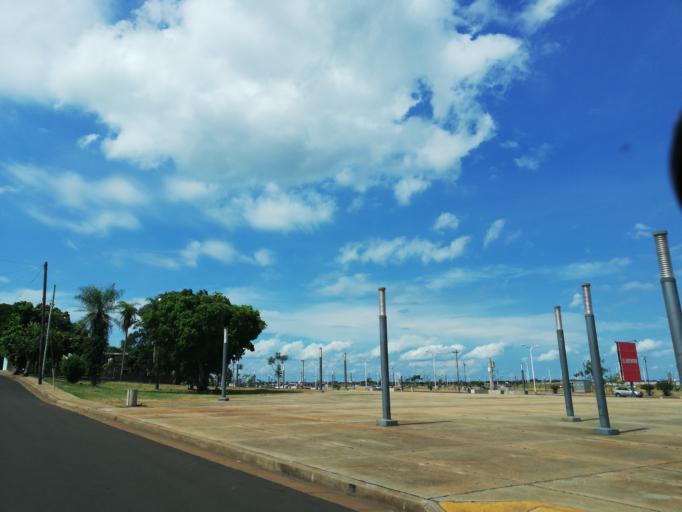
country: AR
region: Misiones
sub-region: Departamento de Capital
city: Posadas
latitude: -27.3787
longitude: -55.8886
